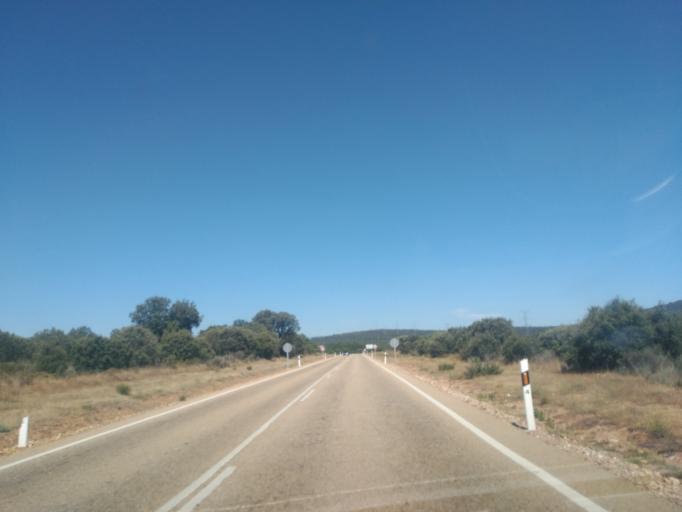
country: ES
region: Castille and Leon
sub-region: Provincia de Zamora
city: Ferreras de Abajo
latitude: 41.8956
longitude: -6.0391
